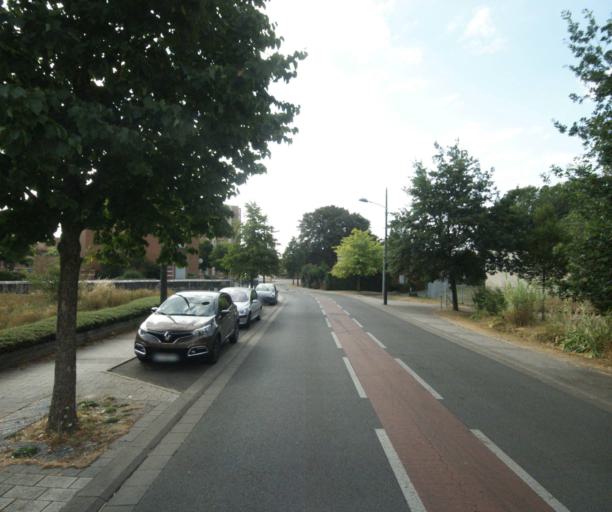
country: FR
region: Nord-Pas-de-Calais
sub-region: Departement du Nord
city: Tourcoing
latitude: 50.7382
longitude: 3.1820
